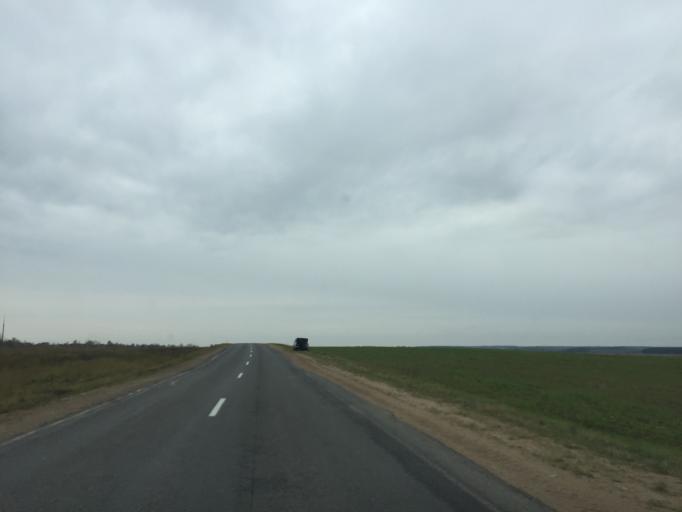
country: BY
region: Mogilev
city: Drybin
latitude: 54.1422
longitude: 31.1160
